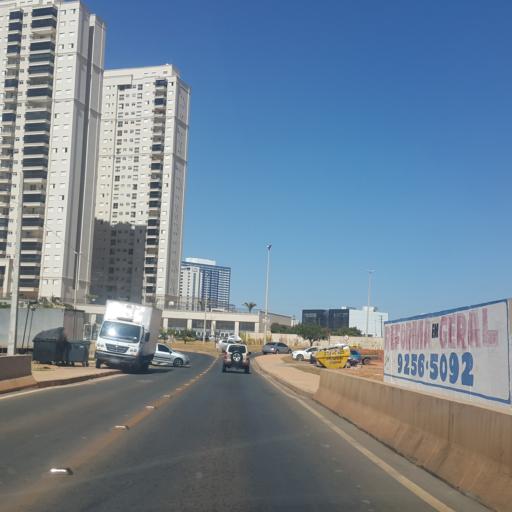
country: BR
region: Federal District
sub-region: Brasilia
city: Brasilia
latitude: -15.8327
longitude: -48.0437
